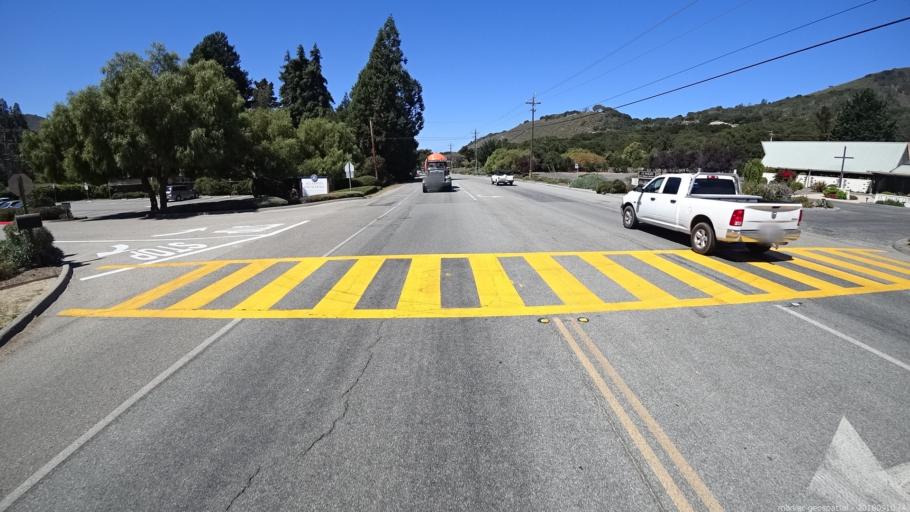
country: US
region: California
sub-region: Monterey County
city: Del Rey Oaks
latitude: 36.5310
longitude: -121.8347
